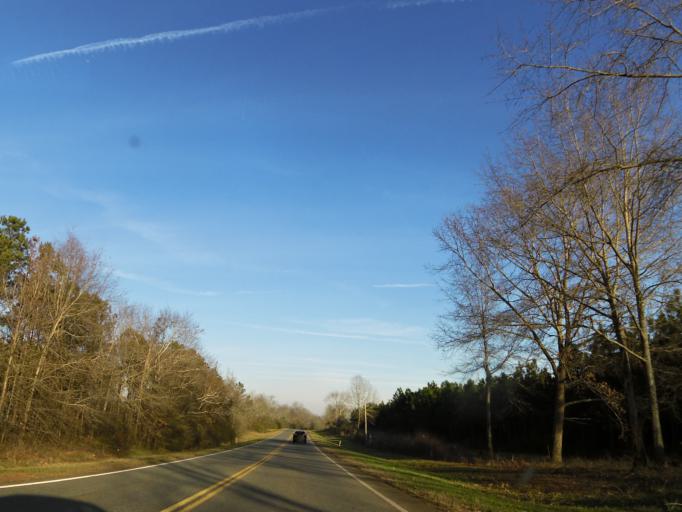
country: US
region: Georgia
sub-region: Sumter County
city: Americus
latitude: 32.0475
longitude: -84.3529
